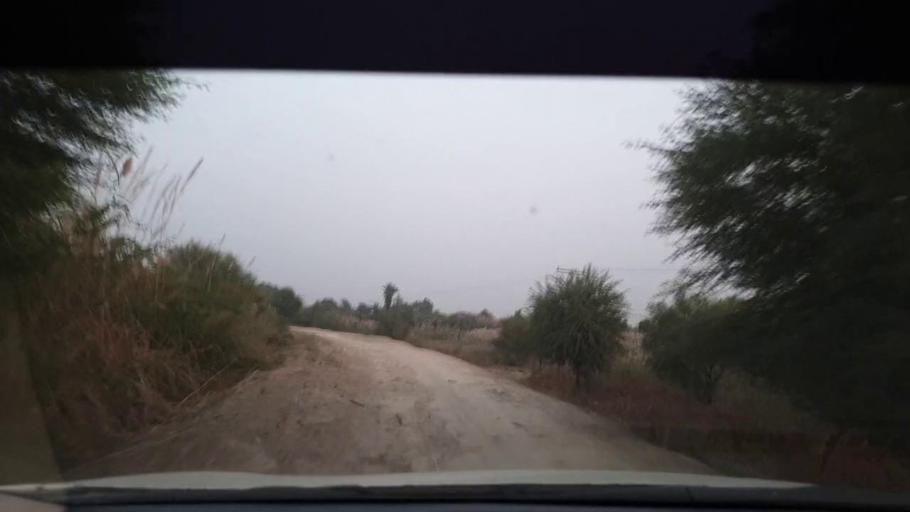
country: PK
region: Sindh
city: Berani
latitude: 25.8457
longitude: 68.7871
